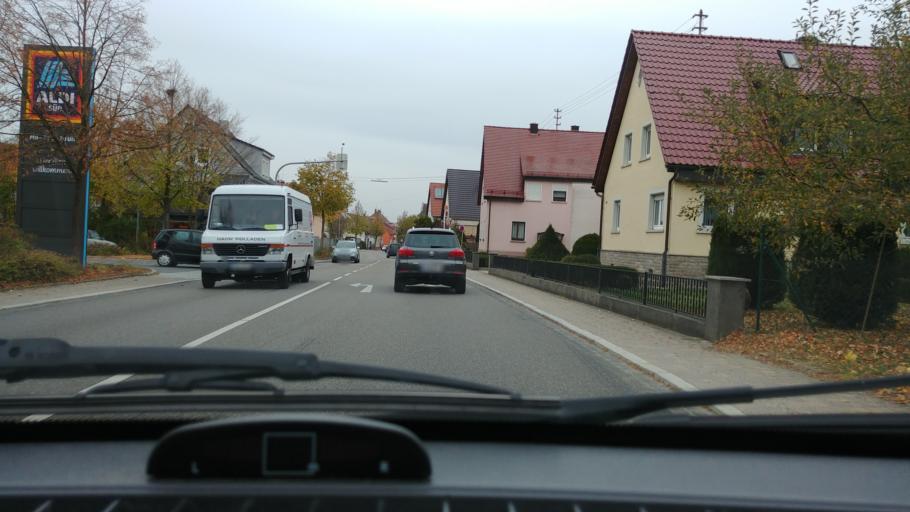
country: DE
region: Baden-Wuerttemberg
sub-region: Regierungsbezirk Stuttgart
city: Lauda-Konigshofen
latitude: 49.5429
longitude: 9.7345
